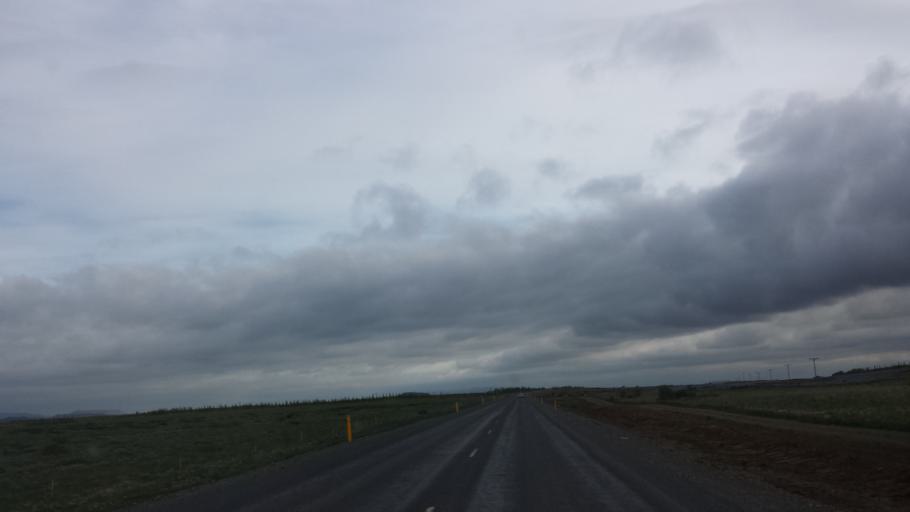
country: IS
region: South
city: Selfoss
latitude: 64.2807
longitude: -20.3454
